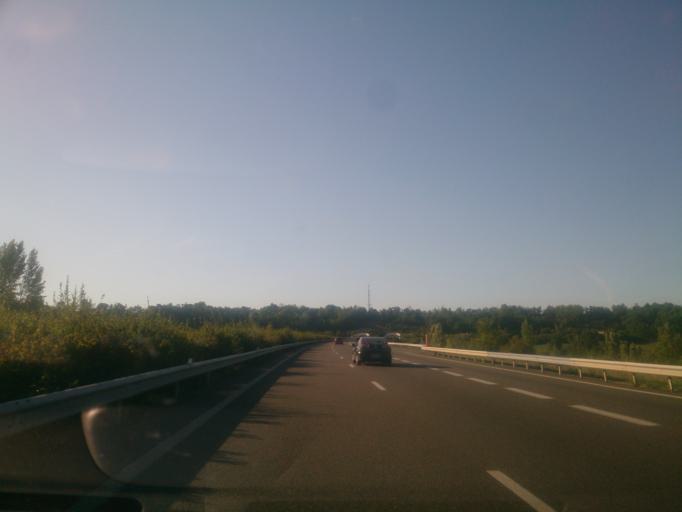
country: FR
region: Midi-Pyrenees
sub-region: Departement du Tarn-et-Garonne
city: Caussade
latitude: 44.2460
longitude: 1.5148
